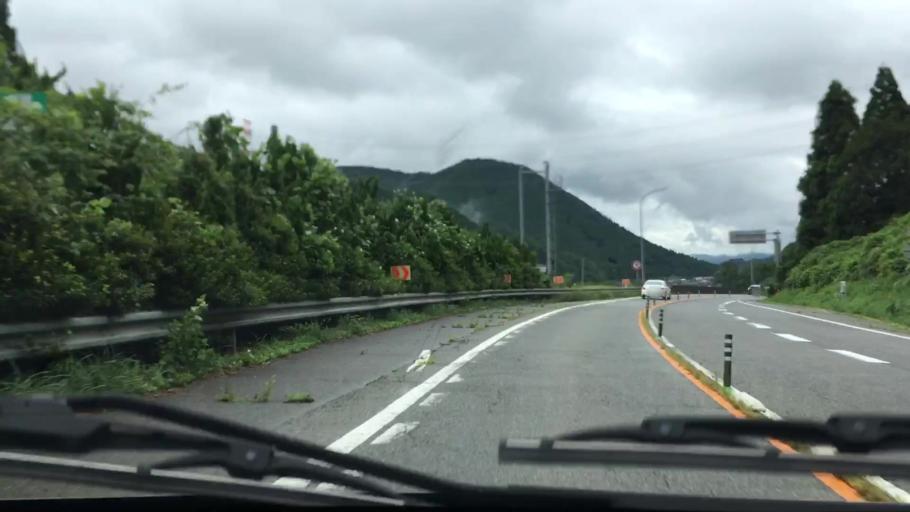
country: JP
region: Hyogo
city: Nishiwaki
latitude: 35.1198
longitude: 134.7865
